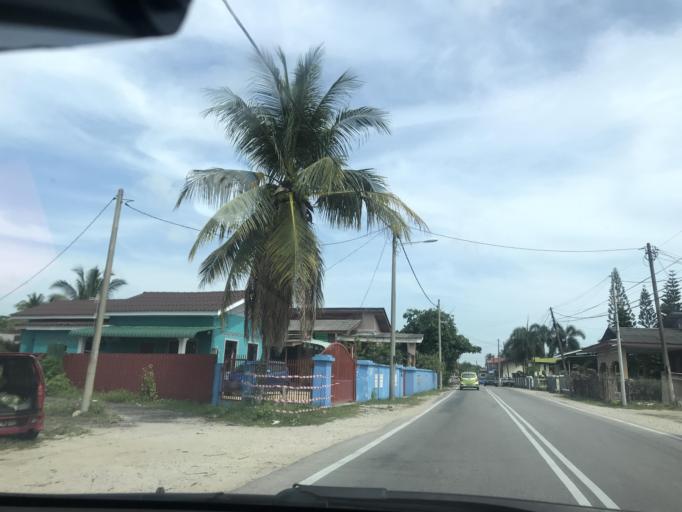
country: MY
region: Kelantan
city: Tumpat
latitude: 6.1998
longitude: 102.1626
